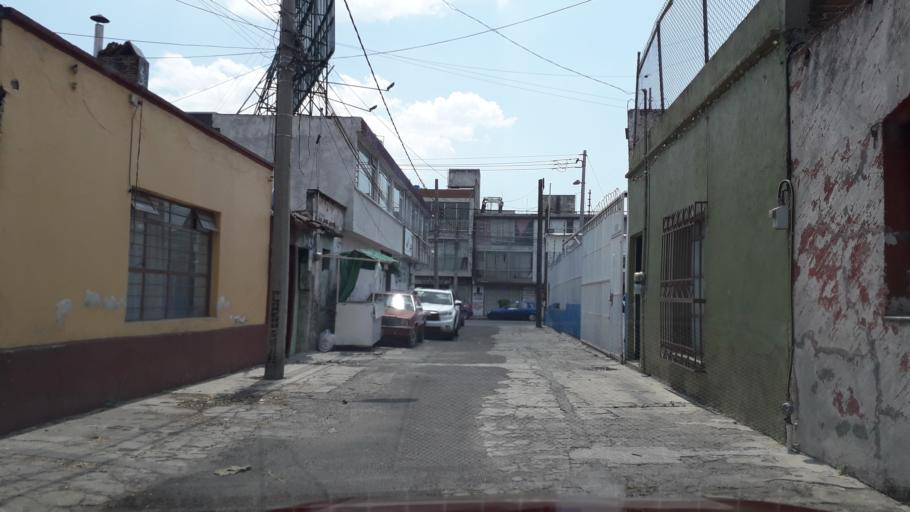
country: MX
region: Puebla
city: Puebla
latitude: 19.0422
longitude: -98.2166
